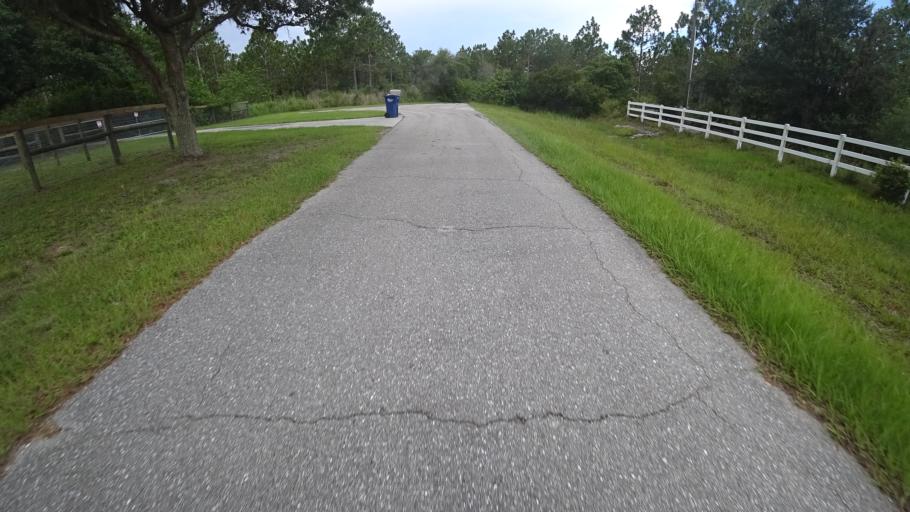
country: US
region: Florida
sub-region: Sarasota County
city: Fruitville
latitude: 27.4106
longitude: -82.2788
